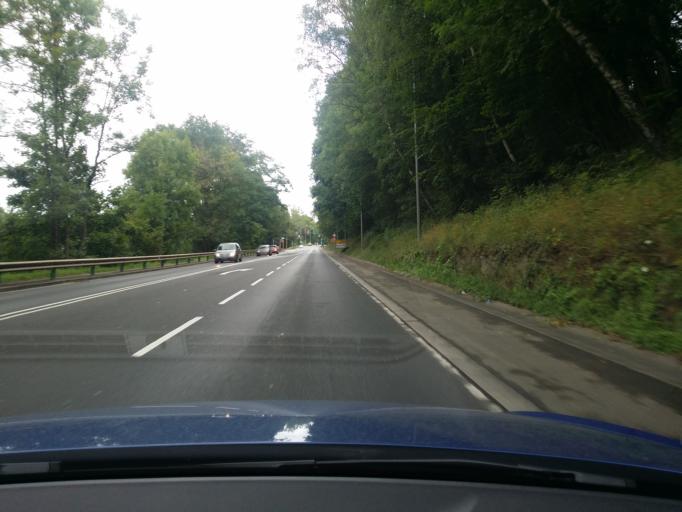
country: LU
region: Luxembourg
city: Kirchberg
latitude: 49.6129
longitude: 6.1608
